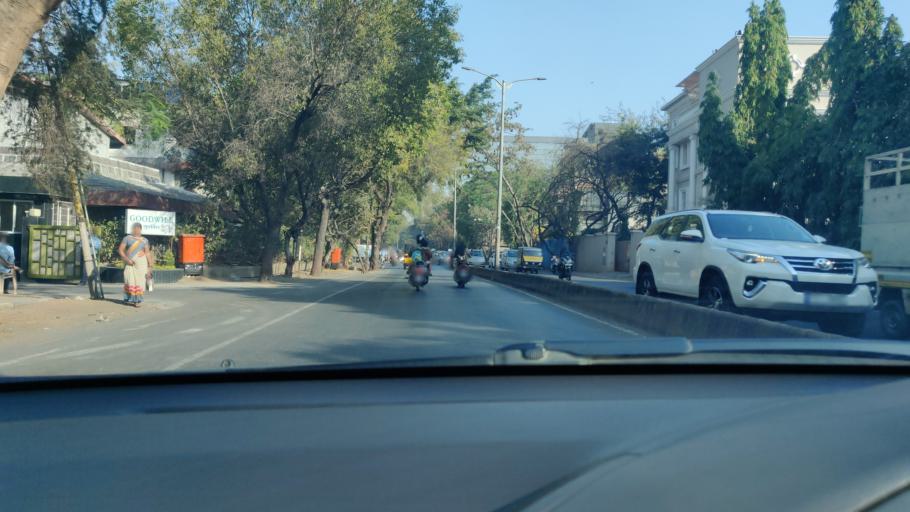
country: IN
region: Maharashtra
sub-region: Pune Division
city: Khadki
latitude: 18.5526
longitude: 73.8095
